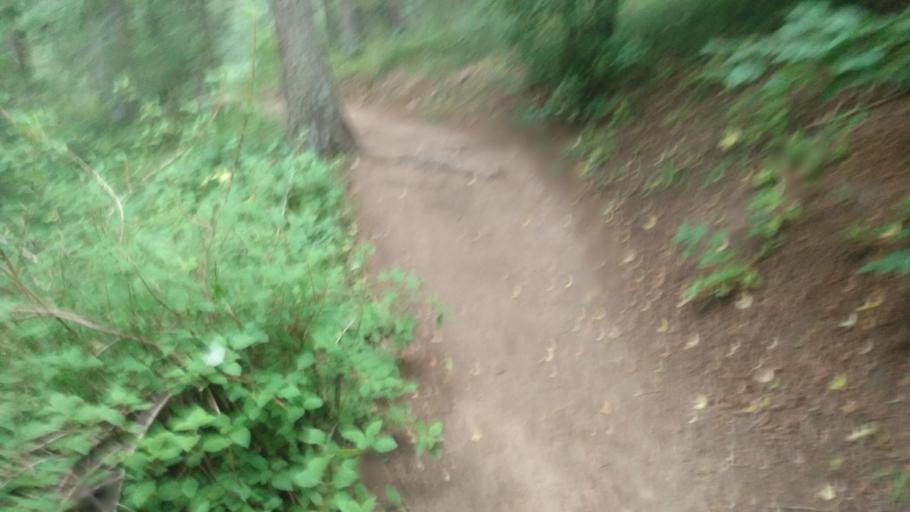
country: US
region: Colorado
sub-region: Boulder County
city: Boulder
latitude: 39.9951
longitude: -105.3084
